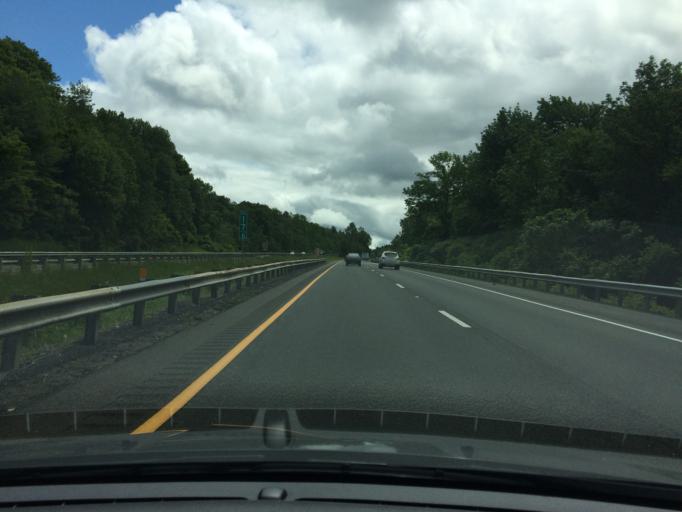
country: US
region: Massachusetts
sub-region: Berkshire County
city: Otis
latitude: 42.2578
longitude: -73.1238
